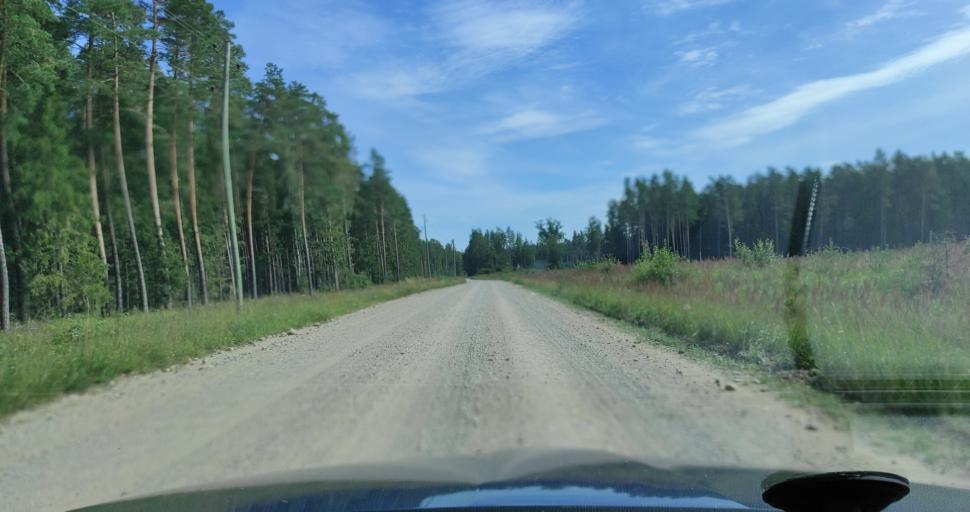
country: LV
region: Durbe
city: Liegi
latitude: 56.7612
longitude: 21.3216
